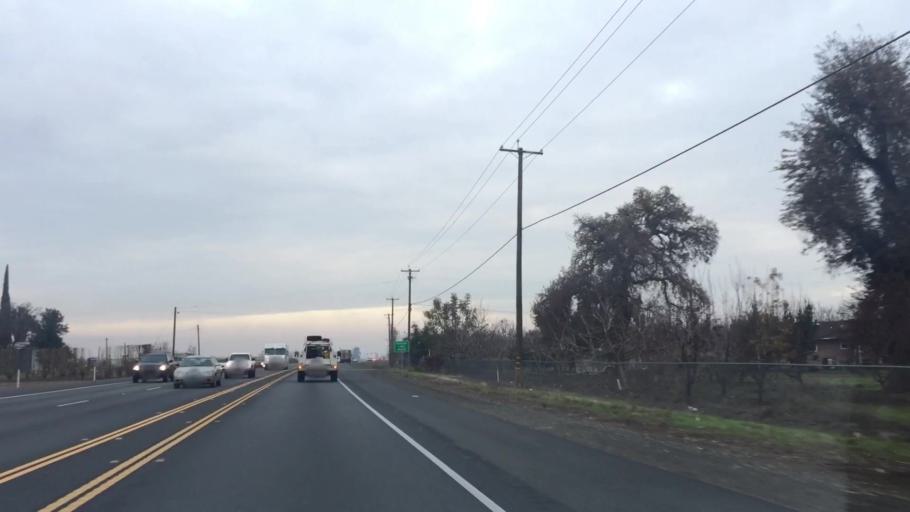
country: US
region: California
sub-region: Butte County
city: Gridley
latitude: 39.3563
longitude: -121.6047
